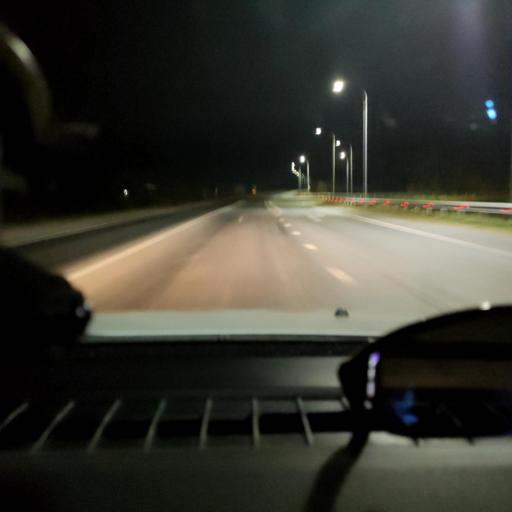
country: RU
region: Samara
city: Samara
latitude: 53.0857
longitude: 50.1421
